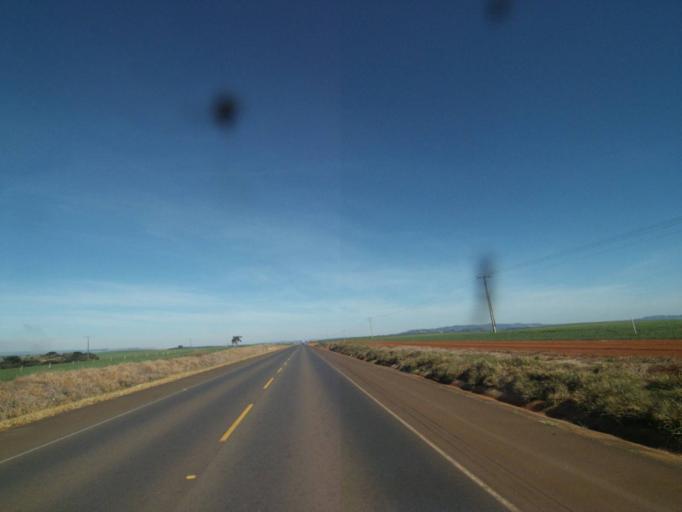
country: BR
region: Parana
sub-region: Tibagi
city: Tibagi
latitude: -24.4432
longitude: -50.4233
